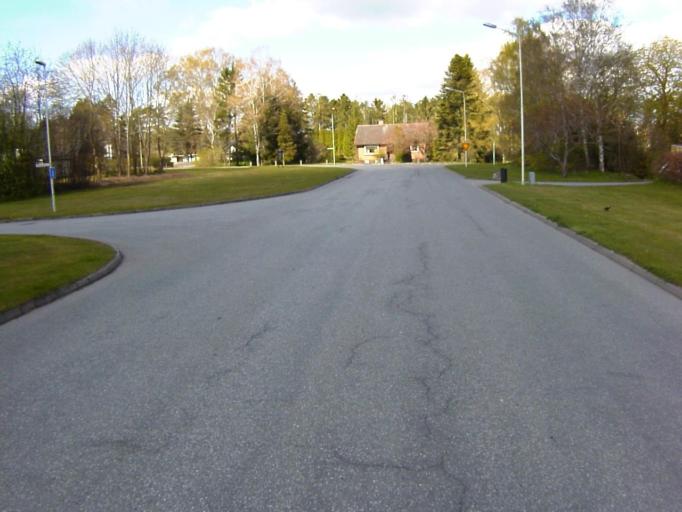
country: SE
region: Skane
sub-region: Kristianstads Kommun
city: Norra Asum
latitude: 56.0049
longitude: 14.0990
